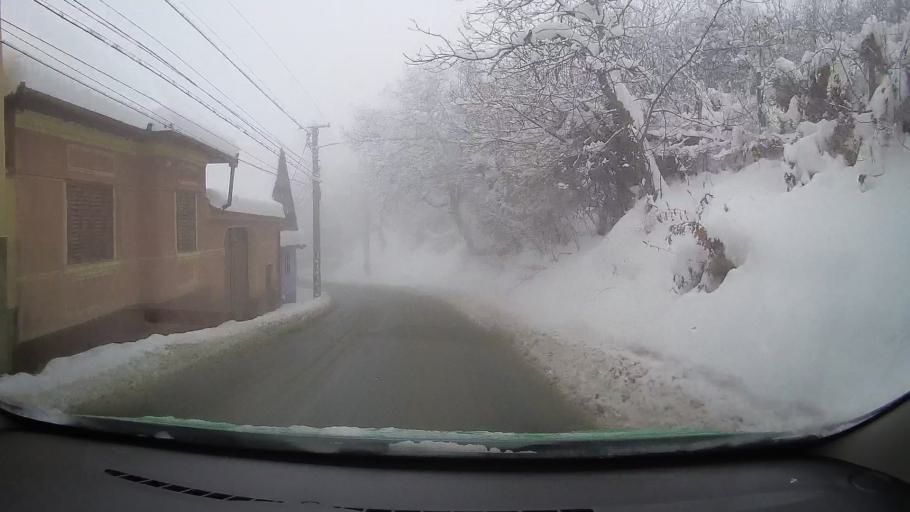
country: RO
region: Sibiu
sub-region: Comuna Poiana Sibiului
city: Poiana Sibiului
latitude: 45.8071
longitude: 23.7375
